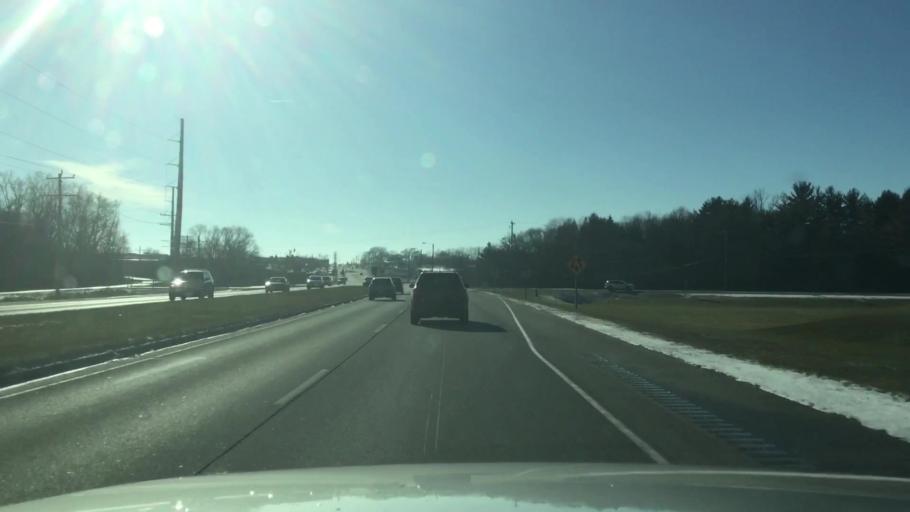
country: US
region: Wisconsin
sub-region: Racine County
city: Burlington
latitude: 42.6980
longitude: -88.2591
